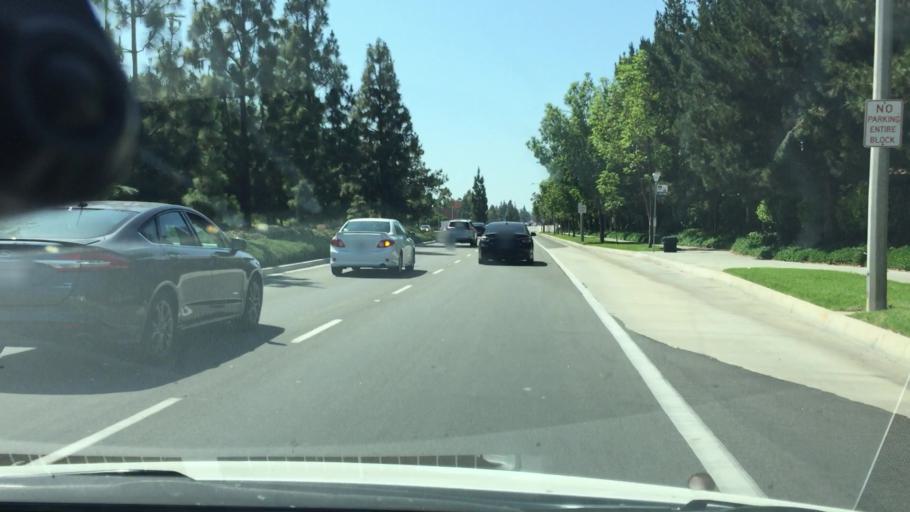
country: US
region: California
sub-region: Orange County
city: North Tustin
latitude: 33.7204
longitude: -117.7827
